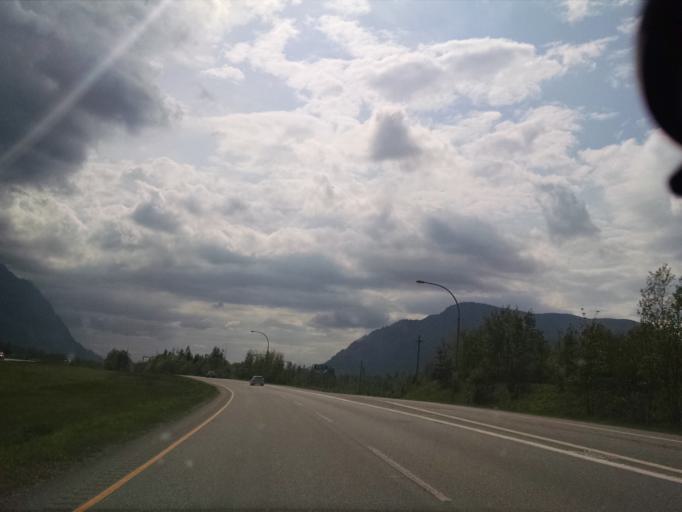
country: CA
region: British Columbia
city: Hope
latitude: 49.3563
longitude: -121.5775
